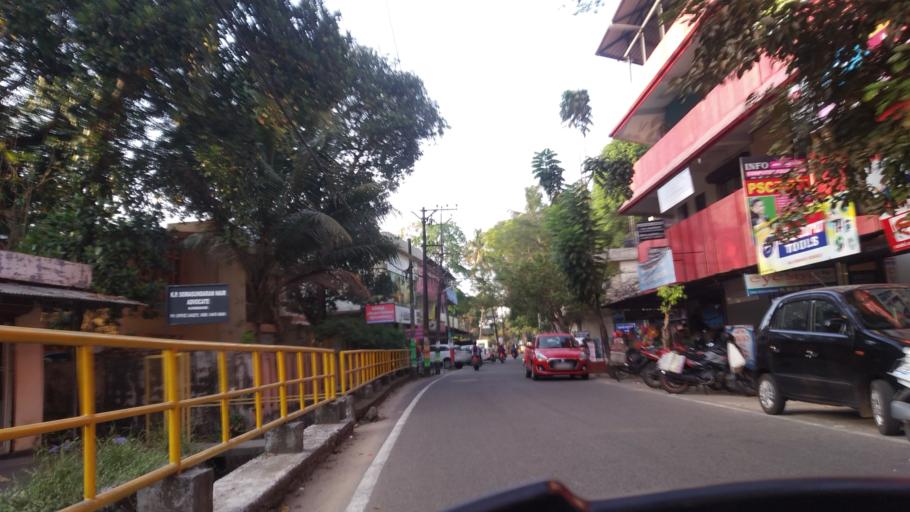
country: IN
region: Kerala
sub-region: Thrissur District
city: Kodungallur
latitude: 10.1463
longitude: 76.2291
